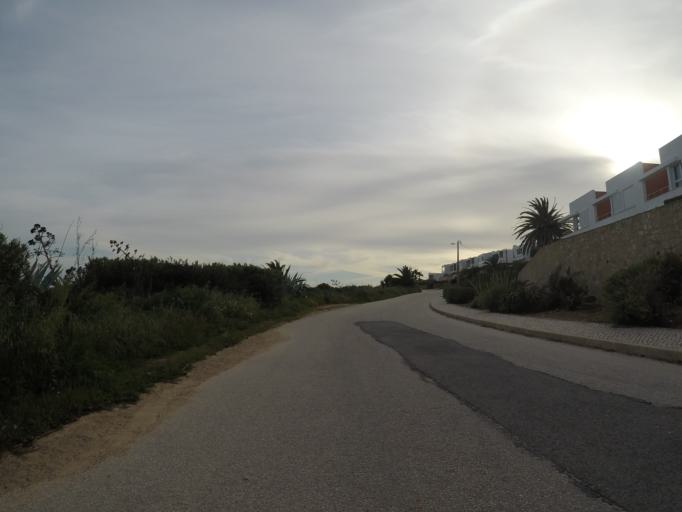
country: PT
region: Faro
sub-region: Lagos
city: Lagos
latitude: 37.0842
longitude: -8.7341
